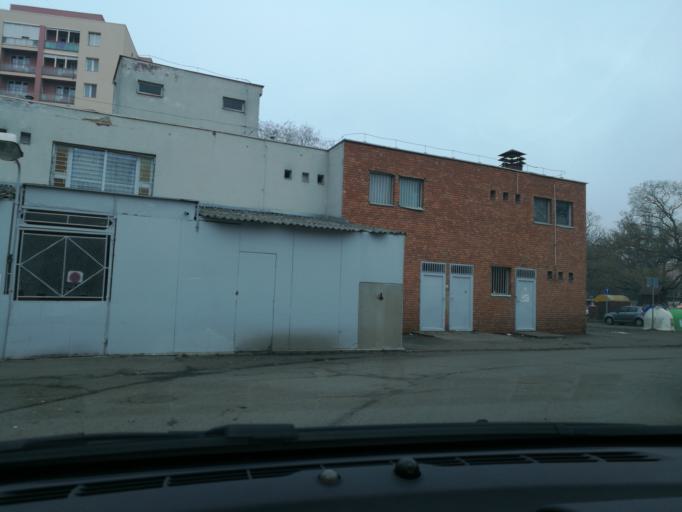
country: HU
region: Szabolcs-Szatmar-Bereg
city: Nyiregyhaza
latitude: 47.9669
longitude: 21.7104
